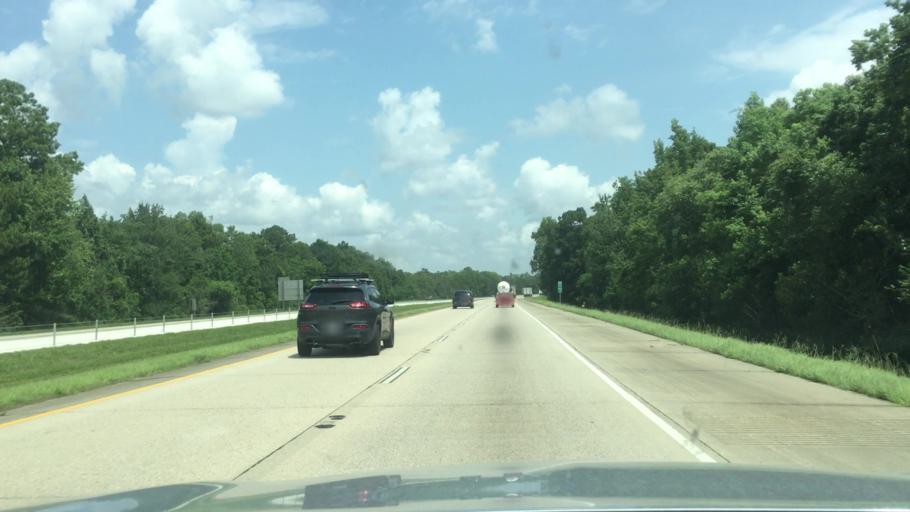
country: US
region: Louisiana
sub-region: Saint Tammany Parish
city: Pearl River
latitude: 30.3626
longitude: -89.7423
